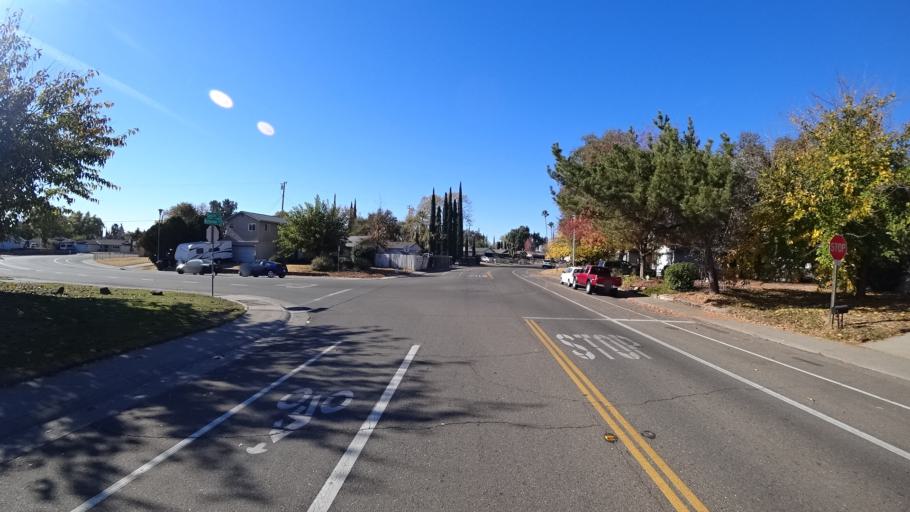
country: US
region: California
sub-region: Sacramento County
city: Antelope
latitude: 38.7172
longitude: -121.3101
